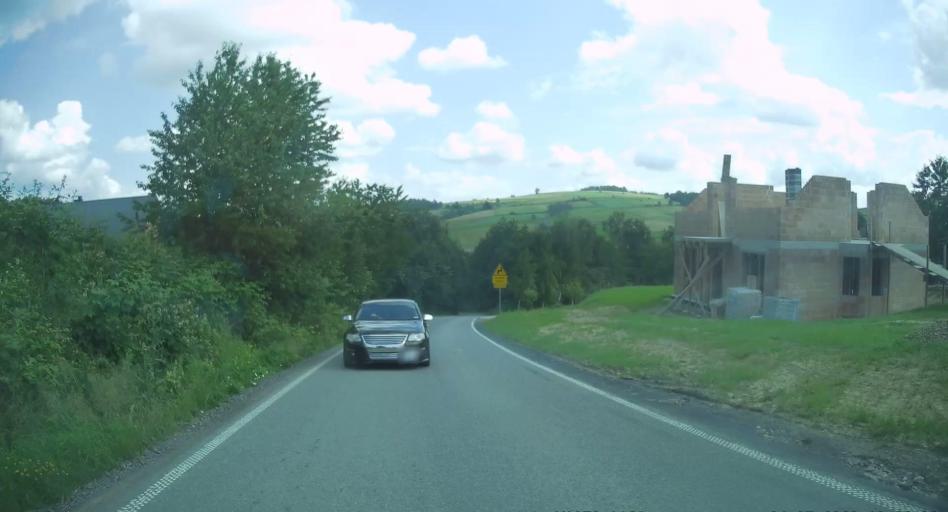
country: PL
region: Lesser Poland Voivodeship
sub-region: Powiat nowosadecki
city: Korzenna
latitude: 49.7112
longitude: 20.7723
